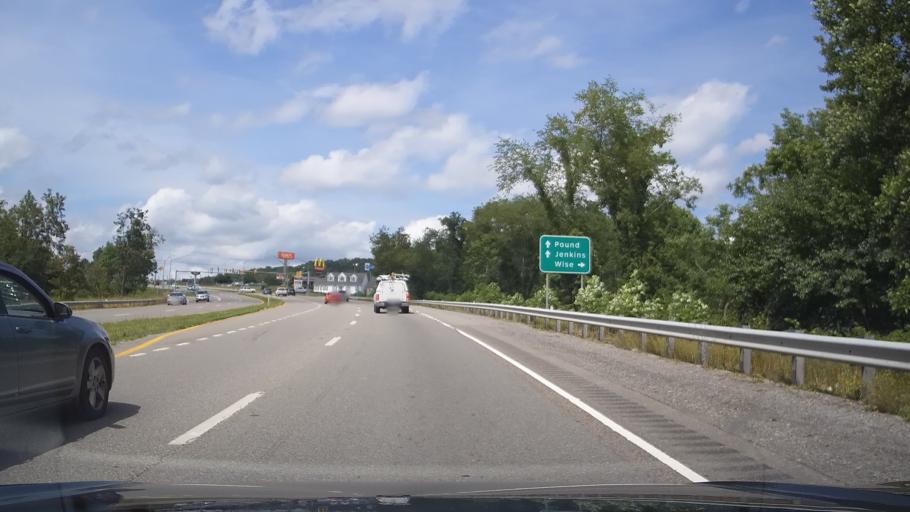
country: US
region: Virginia
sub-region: Wise County
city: Wise
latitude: 36.9664
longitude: -82.5968
